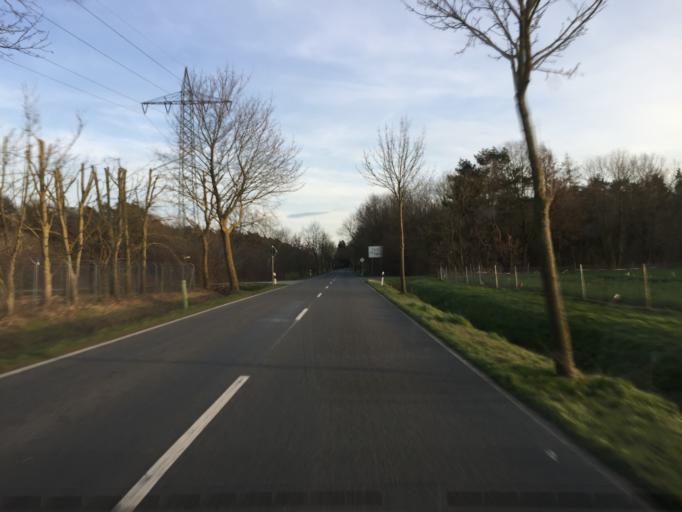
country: DE
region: Lower Saxony
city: Neustadt am Rubenberge
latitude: 52.4953
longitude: 9.4872
